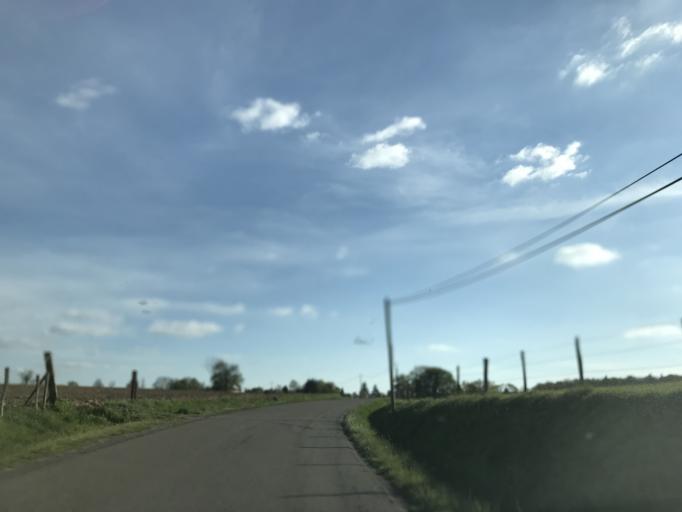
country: FR
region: Auvergne
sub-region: Departement du Puy-de-Dome
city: Montaigut
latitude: 45.7027
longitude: 3.4415
